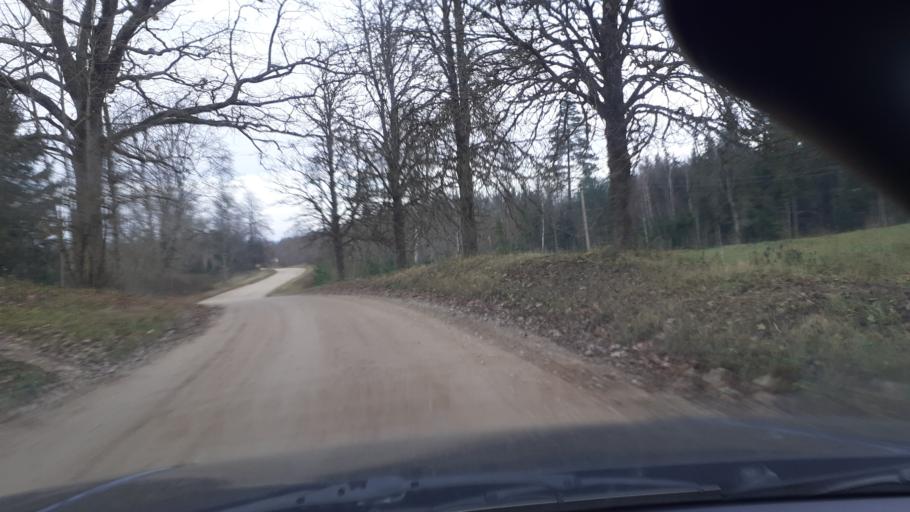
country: LV
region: Alsunga
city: Alsunga
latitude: 56.9732
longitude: 21.6671
